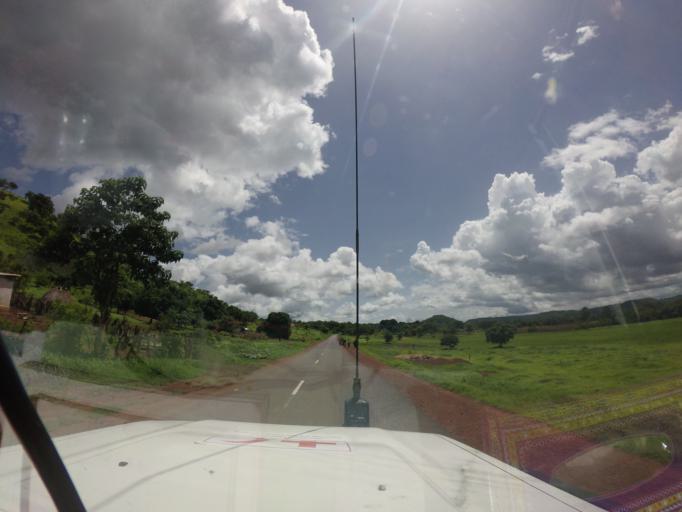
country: SL
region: Northern Province
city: Bindi
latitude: 10.1473
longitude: -11.6102
